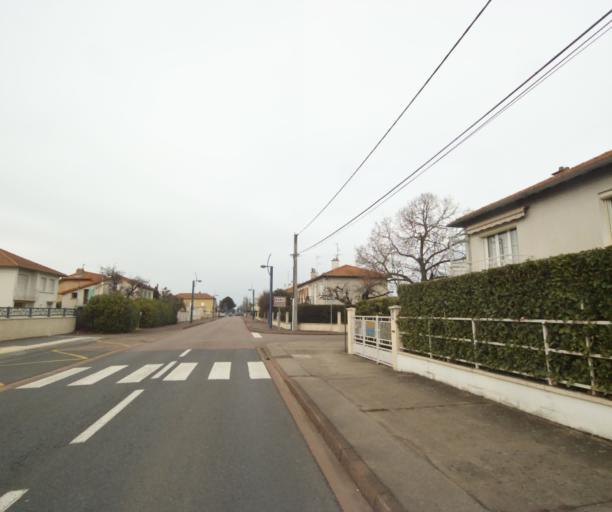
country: FR
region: Rhone-Alpes
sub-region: Departement de la Loire
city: Mably
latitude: 46.0680
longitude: 4.0740
